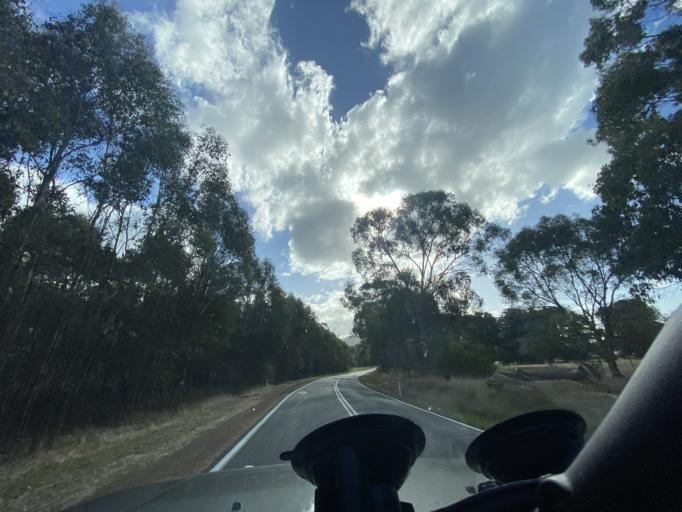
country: AU
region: Victoria
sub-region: Murrindindi
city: Kinglake West
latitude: -37.3221
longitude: 145.3014
